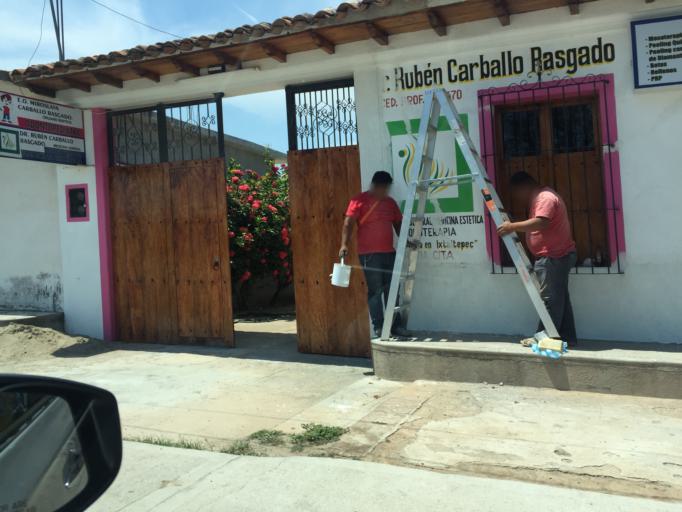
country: MX
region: Oaxaca
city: Asuncion Ixtaltepec
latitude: 16.5044
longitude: -95.0624
